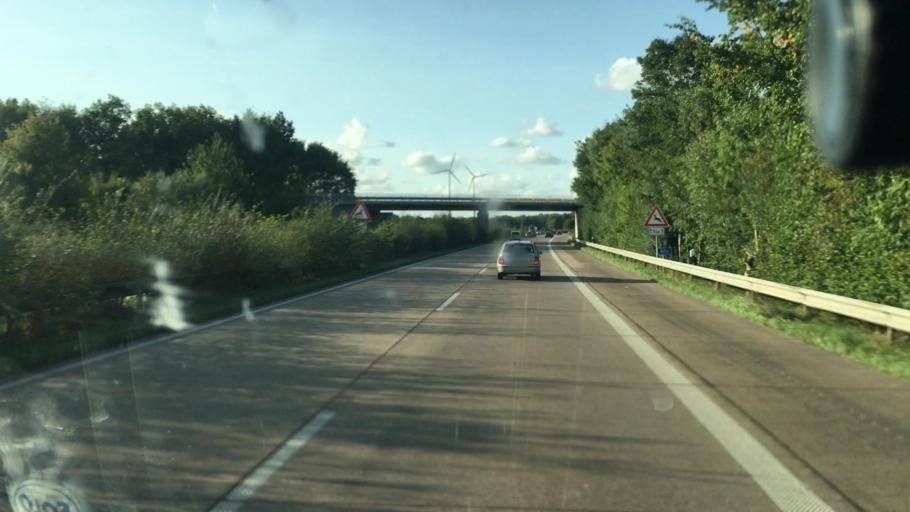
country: DE
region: Lower Saxony
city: Sande
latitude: 53.4900
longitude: 8.0018
